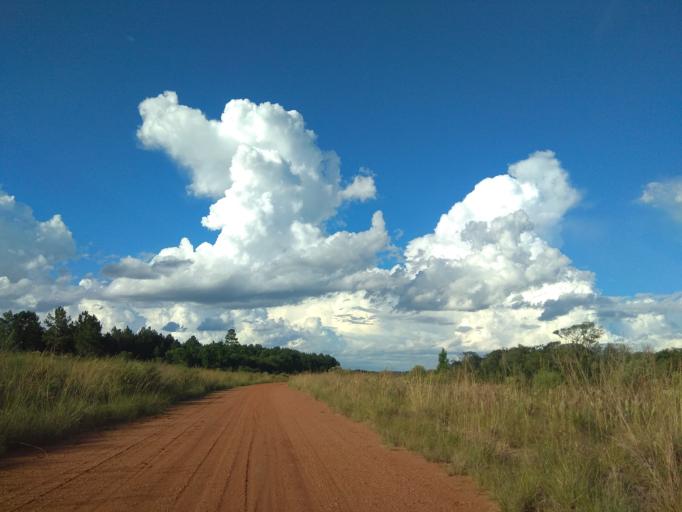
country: AR
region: Misiones
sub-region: Departamento de Candelaria
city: Candelaria
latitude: -27.4947
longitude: -55.7628
